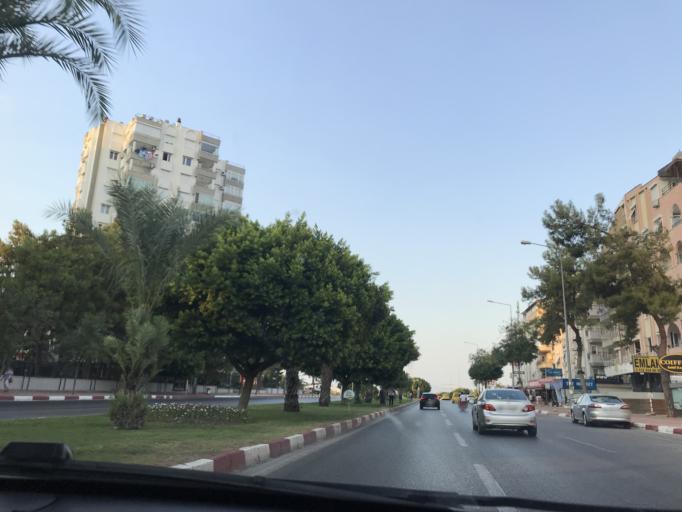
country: TR
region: Antalya
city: Antalya
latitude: 36.8673
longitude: 30.6373
